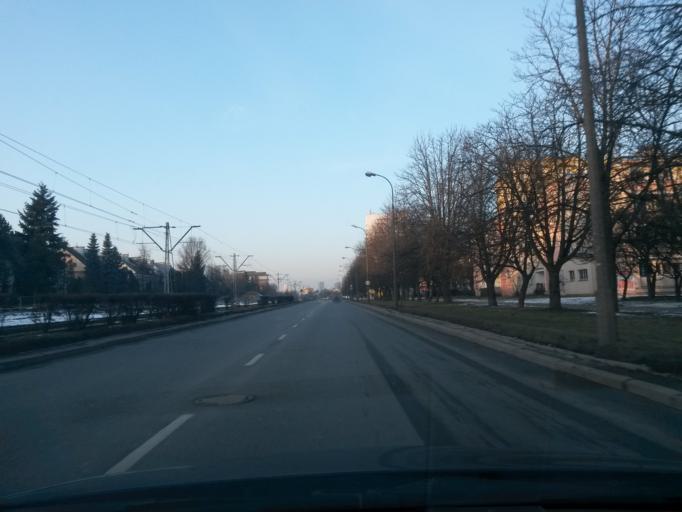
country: PL
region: Masovian Voivodeship
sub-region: Warszawa
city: Mokotow
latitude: 52.1910
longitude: 21.0020
